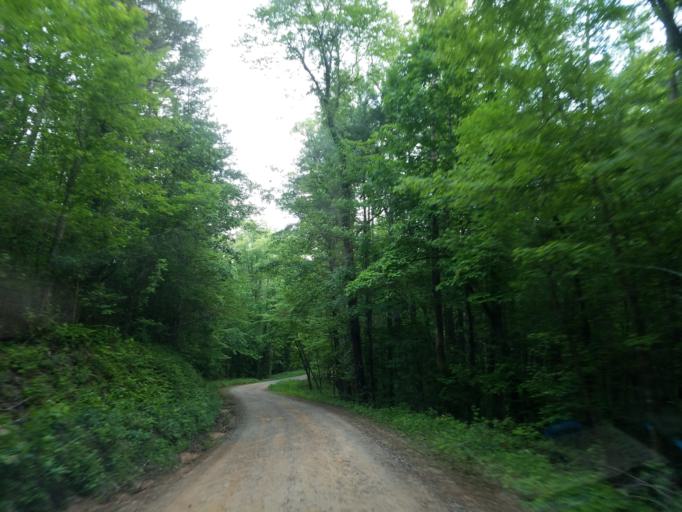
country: US
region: Georgia
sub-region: Lumpkin County
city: Dahlonega
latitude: 34.5890
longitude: -84.1208
